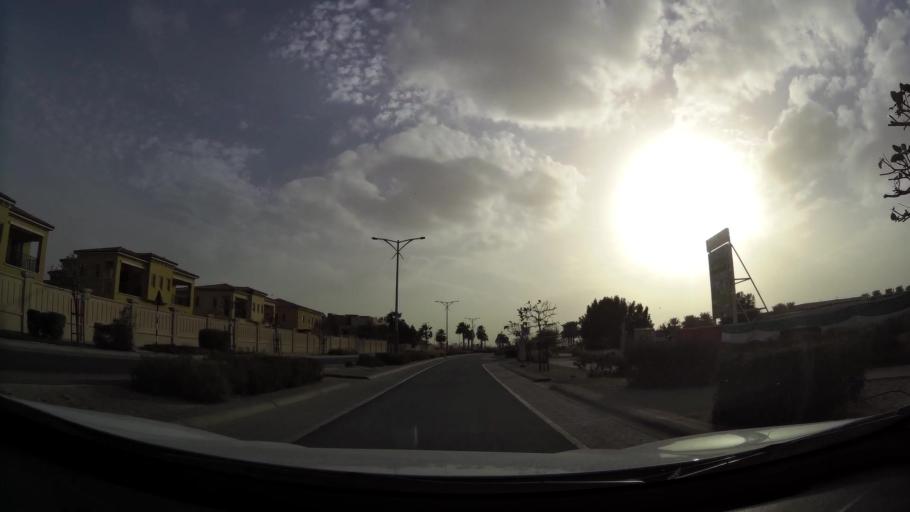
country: AE
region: Abu Dhabi
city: Abu Dhabi
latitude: 24.5584
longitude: 54.4517
